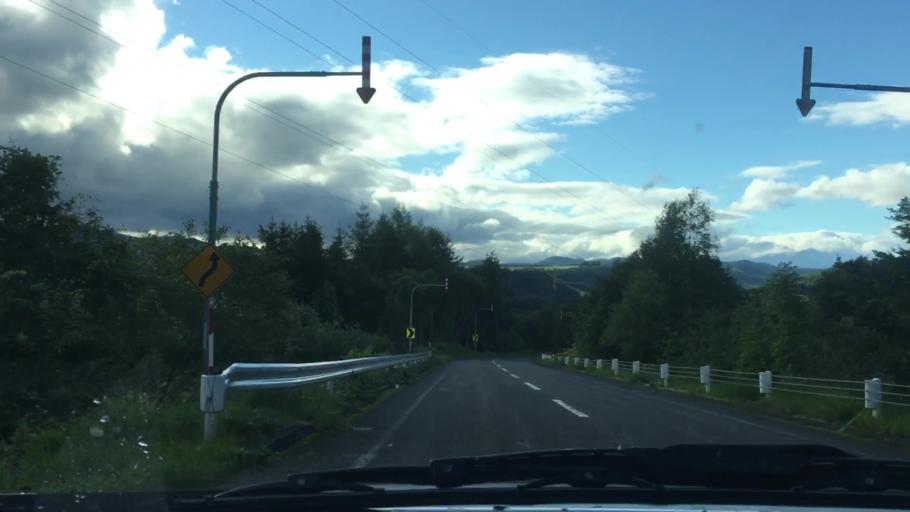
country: JP
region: Hokkaido
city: Otofuke
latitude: 43.1735
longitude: 142.9309
